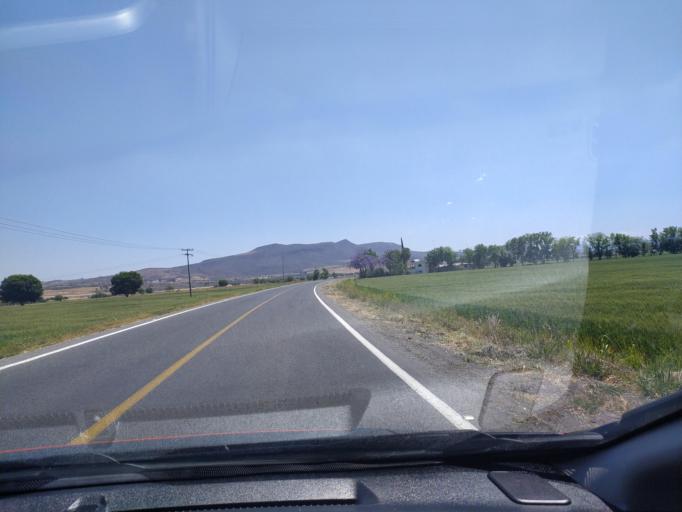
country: MX
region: Guanajuato
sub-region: San Francisco del Rincon
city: San Ignacio de Hidalgo
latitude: 20.8497
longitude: -101.8514
